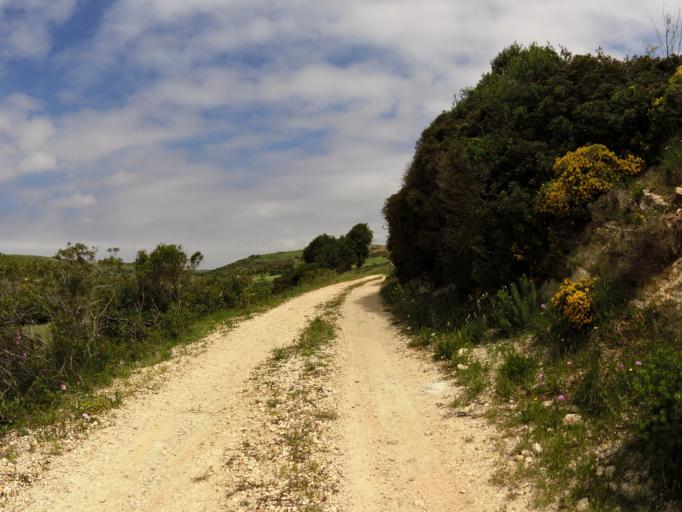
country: PT
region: Faro
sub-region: Vila do Bispo
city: Vila do Bispo
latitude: 37.0710
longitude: -8.8727
